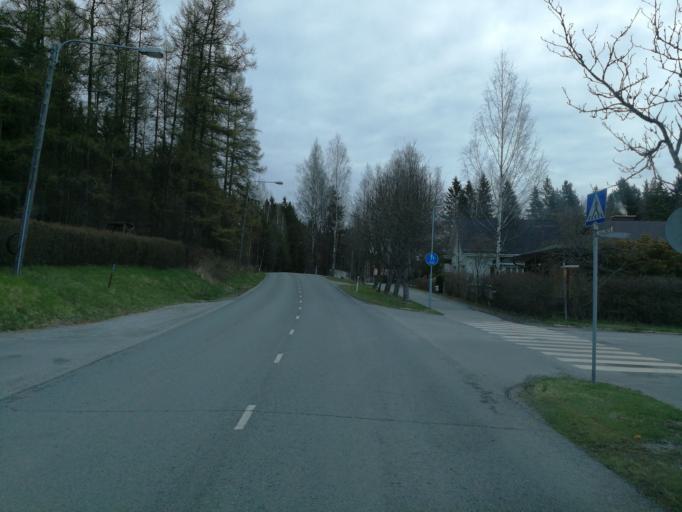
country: FI
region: Varsinais-Suomi
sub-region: Salo
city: Halikko
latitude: 60.3999
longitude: 23.1107
